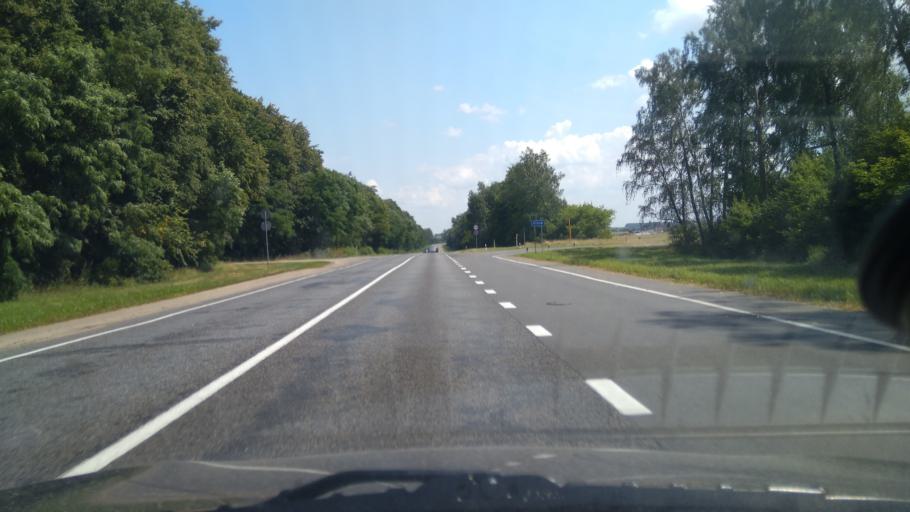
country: BY
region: Brest
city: Baranovichi
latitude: 53.1181
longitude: 26.1414
